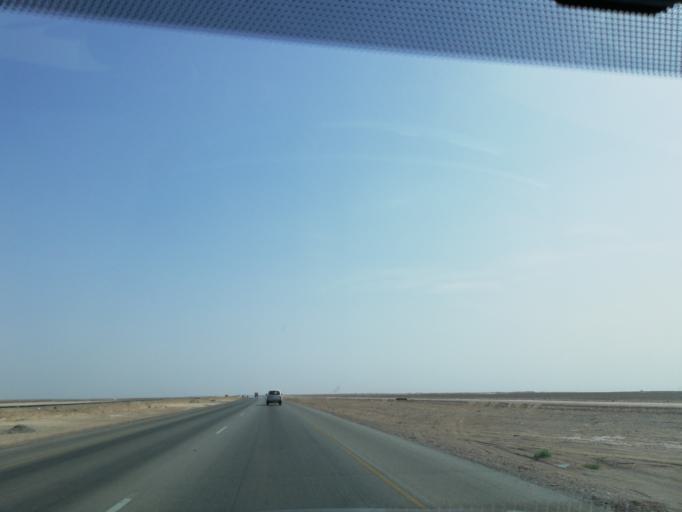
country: OM
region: Muhafazat ad Dakhiliyah
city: Adam
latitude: 21.6060
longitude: 57.2960
